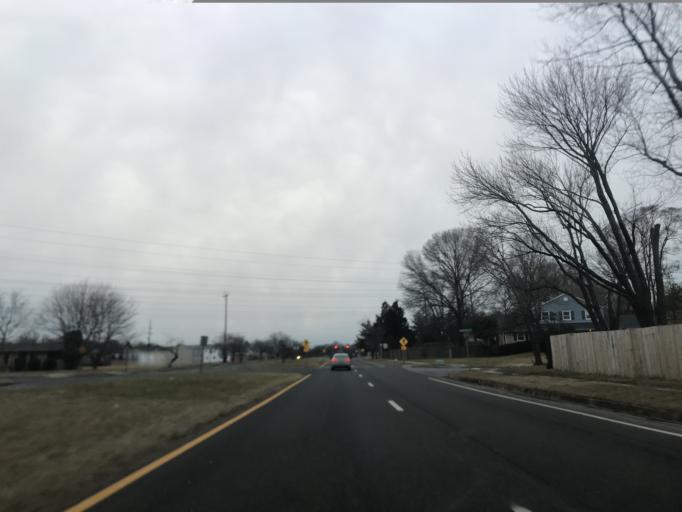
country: US
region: Maryland
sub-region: Prince George's County
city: Kettering
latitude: 38.8956
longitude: -76.7882
